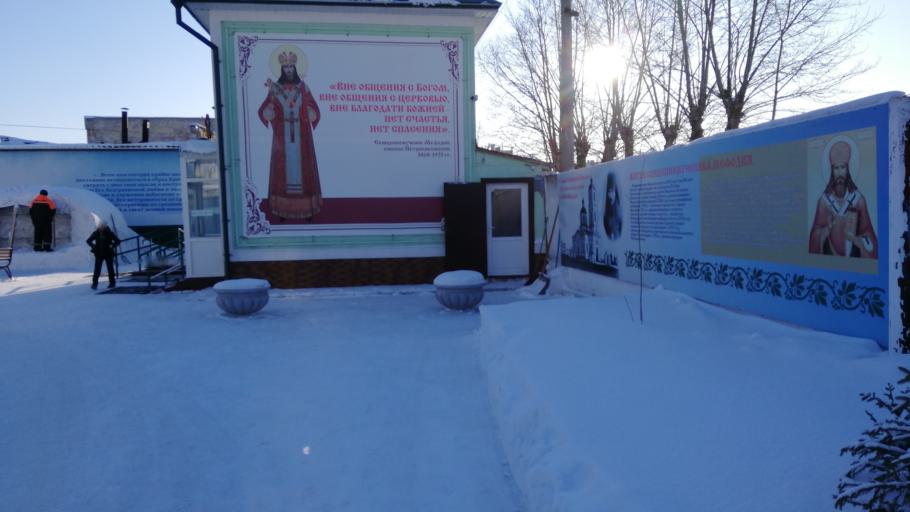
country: KZ
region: Soltustik Qazaqstan
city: Petropavlovsk
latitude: 54.8585
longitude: 69.1599
